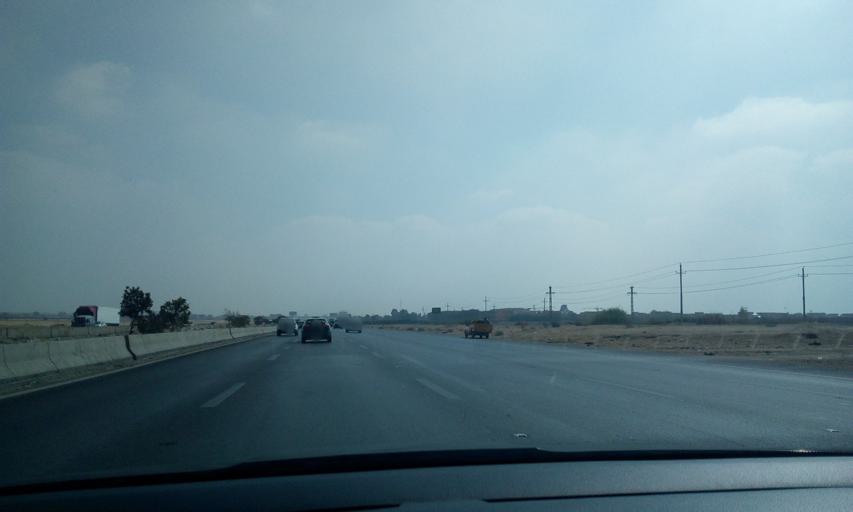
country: EG
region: Eastern Province
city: Bilbays
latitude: 30.2114
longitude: 31.6775
